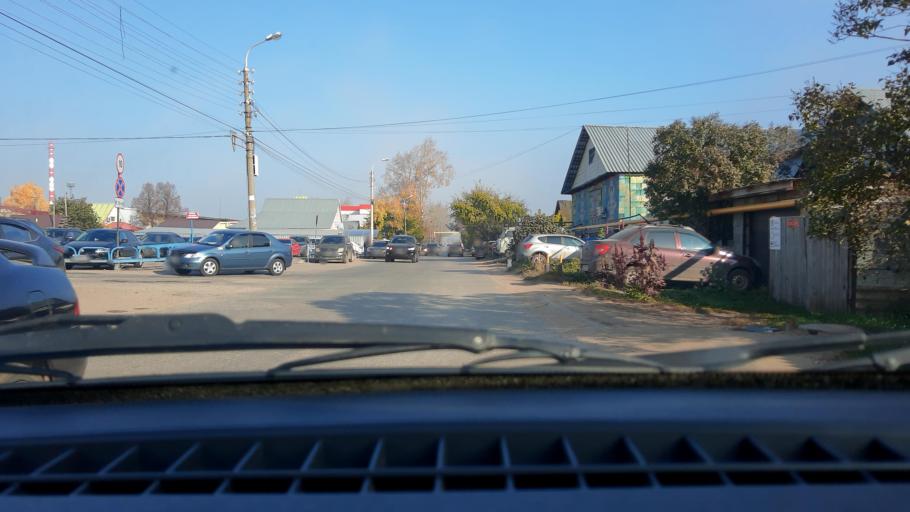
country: RU
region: Bashkortostan
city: Mikhaylovka
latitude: 54.6944
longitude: 55.8493
